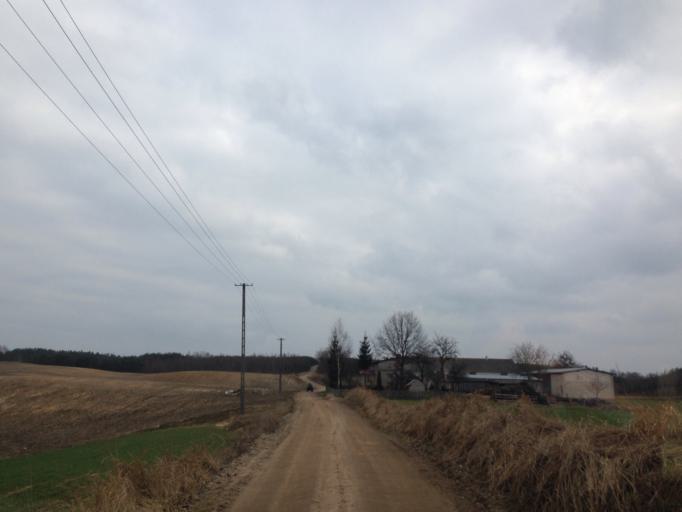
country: PL
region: Warmian-Masurian Voivodeship
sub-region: Powiat dzialdowski
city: Lidzbark
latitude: 53.3702
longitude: 19.7576
